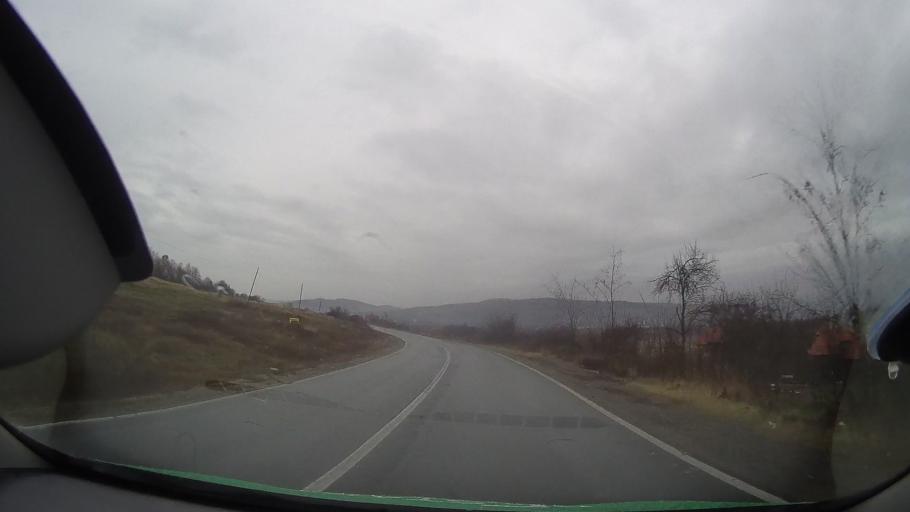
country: RO
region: Bihor
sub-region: Comuna Rabagani
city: Rabagani
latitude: 46.7384
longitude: 22.2301
